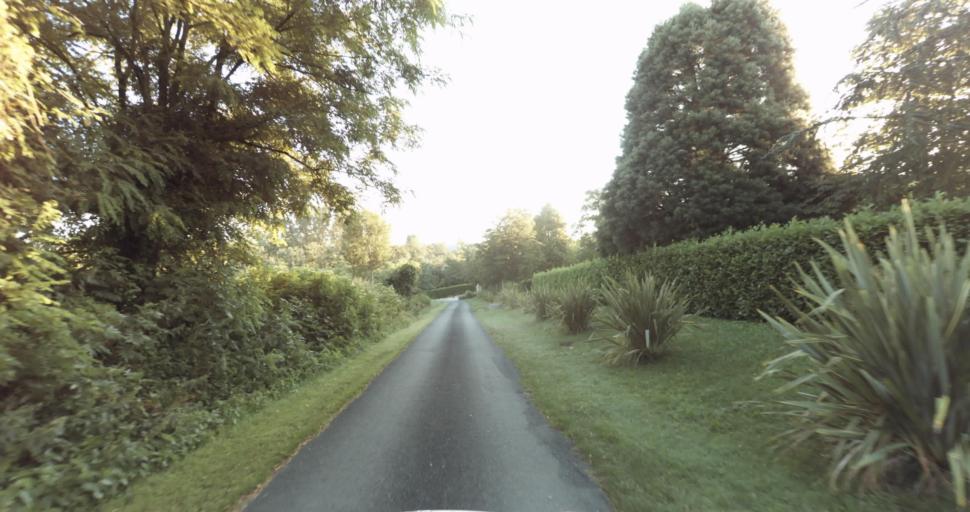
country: FR
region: Aquitaine
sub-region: Departement de la Gironde
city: Bazas
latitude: 44.4285
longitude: -0.2225
